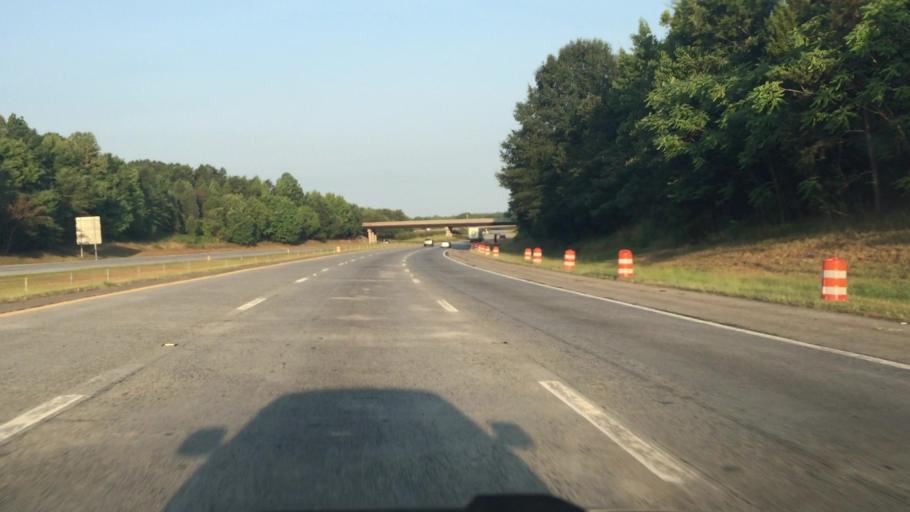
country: US
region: North Carolina
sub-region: Davidson County
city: Thomasville
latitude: 35.8554
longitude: -80.0926
